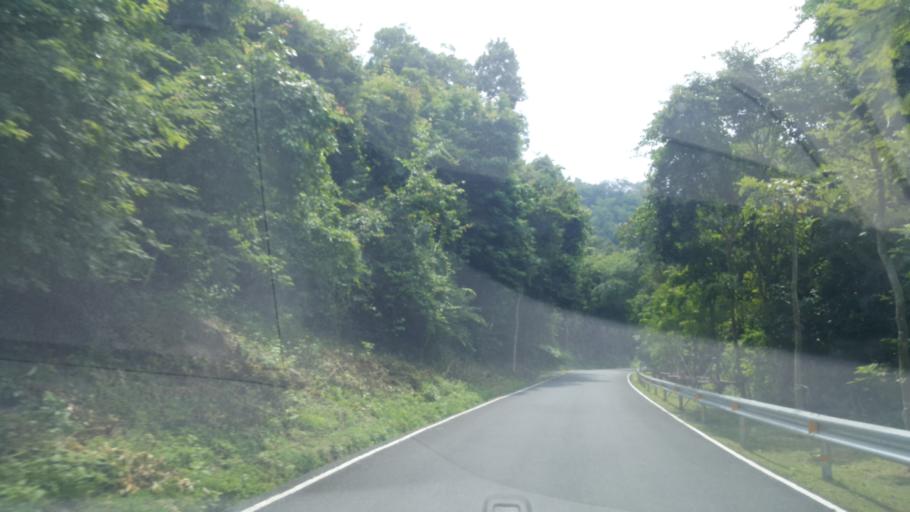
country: TH
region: Chon Buri
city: Ban Bueng
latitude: 13.2101
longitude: 101.0595
